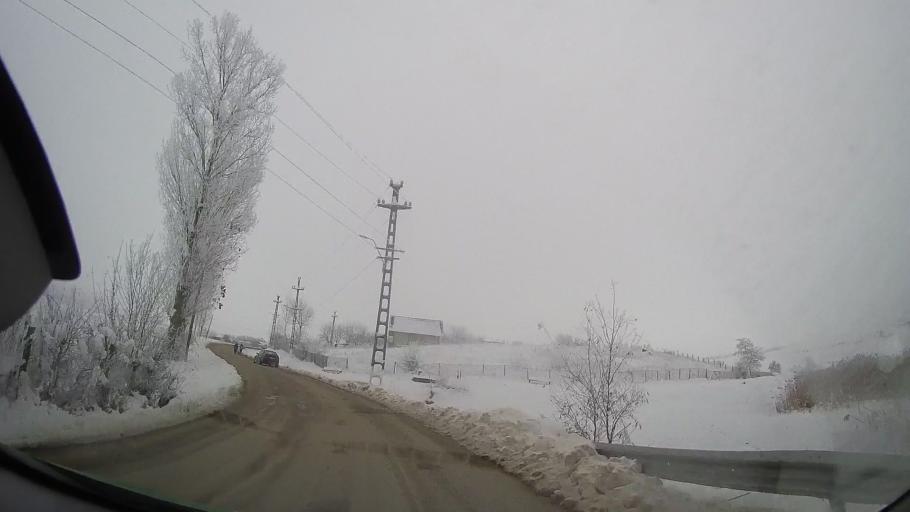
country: RO
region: Iasi
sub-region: Comuna Dagata
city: Dagata
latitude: 46.9156
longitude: 27.1978
